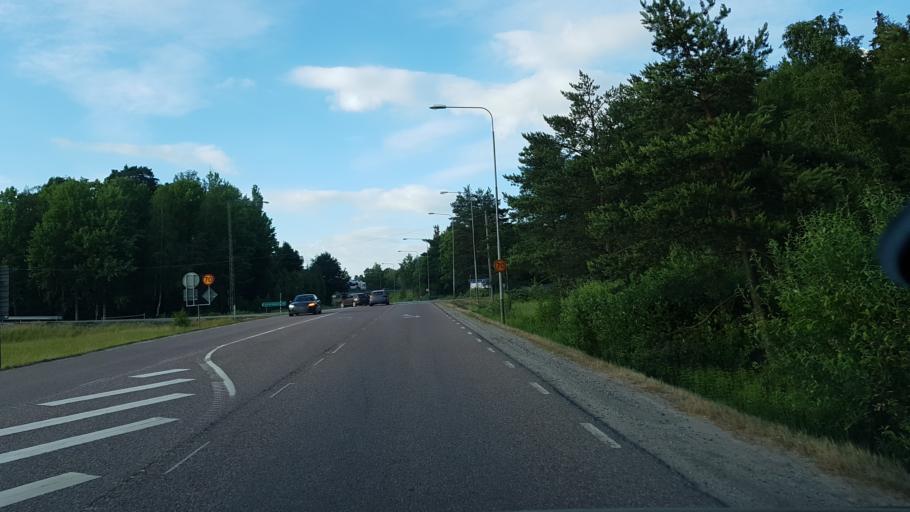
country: SE
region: Stockholm
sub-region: Salems Kommun
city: Ronninge
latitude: 59.2103
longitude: 17.7533
